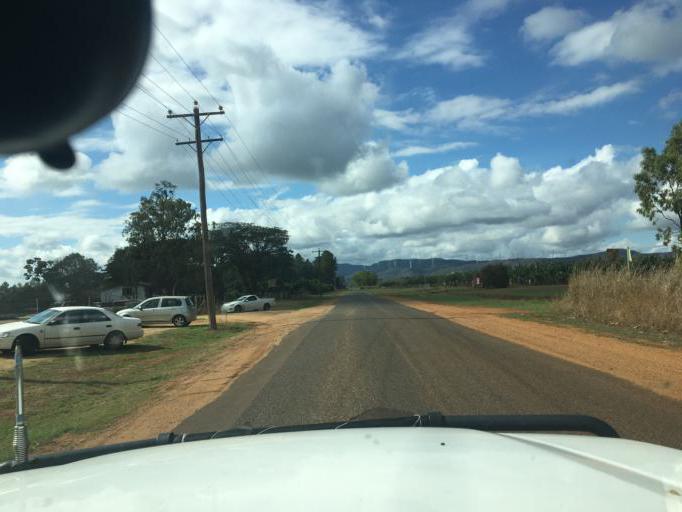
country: AU
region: Queensland
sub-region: Tablelands
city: Mareeba
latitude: -17.1030
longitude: 145.4115
